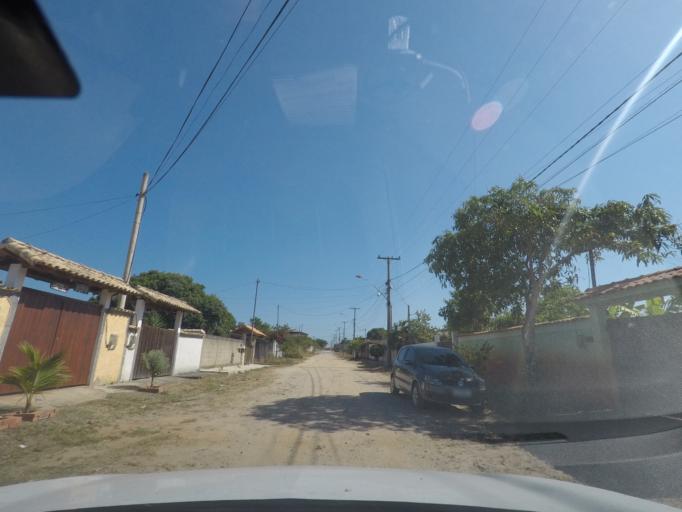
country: BR
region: Rio de Janeiro
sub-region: Marica
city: Marica
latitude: -22.9657
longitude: -42.9083
